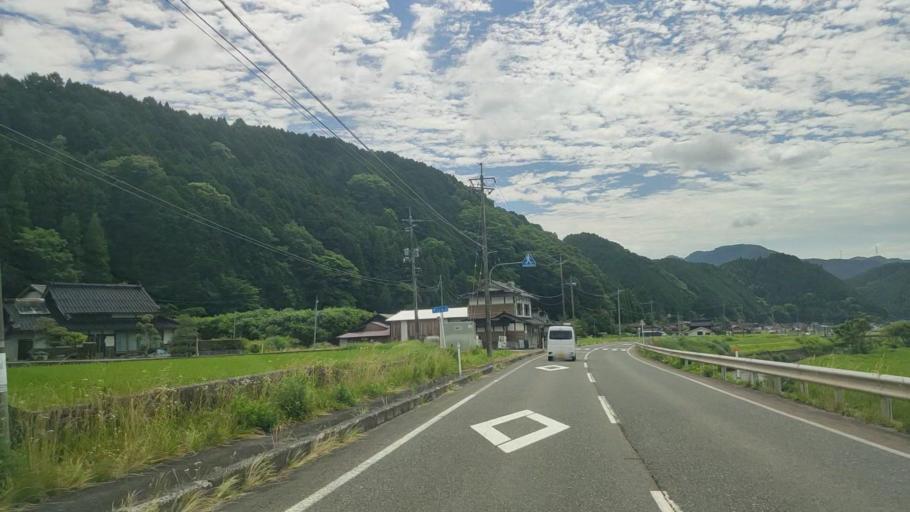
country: JP
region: Okayama
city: Niimi
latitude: 35.1630
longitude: 133.6056
